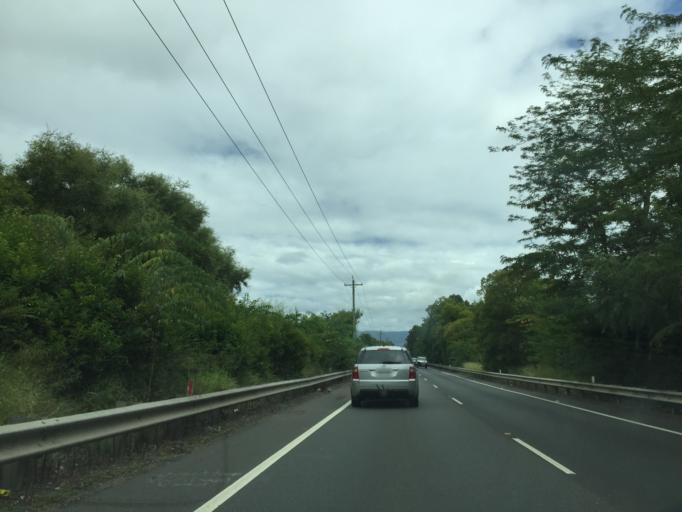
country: AU
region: New South Wales
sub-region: Hawkesbury
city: Richmond
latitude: -33.5938
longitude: 150.7405
